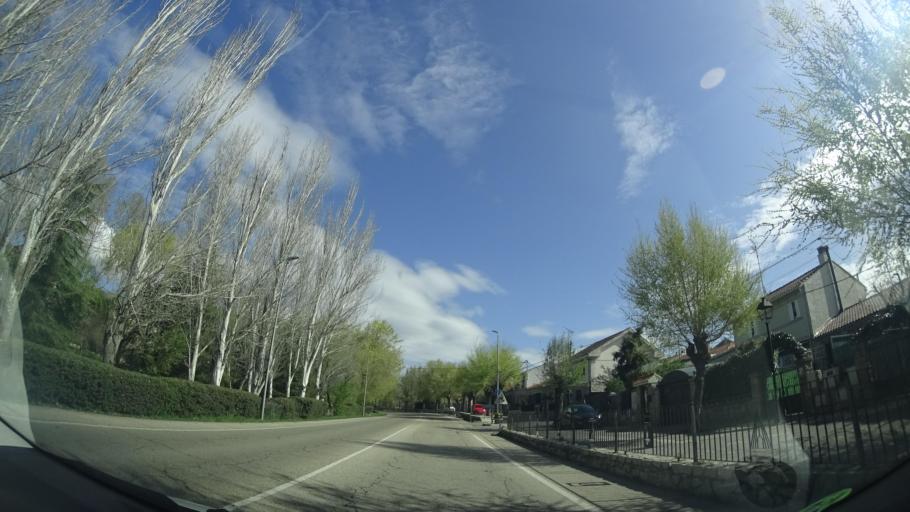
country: ES
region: Madrid
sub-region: Provincia de Madrid
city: Miraflores de la Sierra
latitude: 40.7514
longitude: -3.7822
